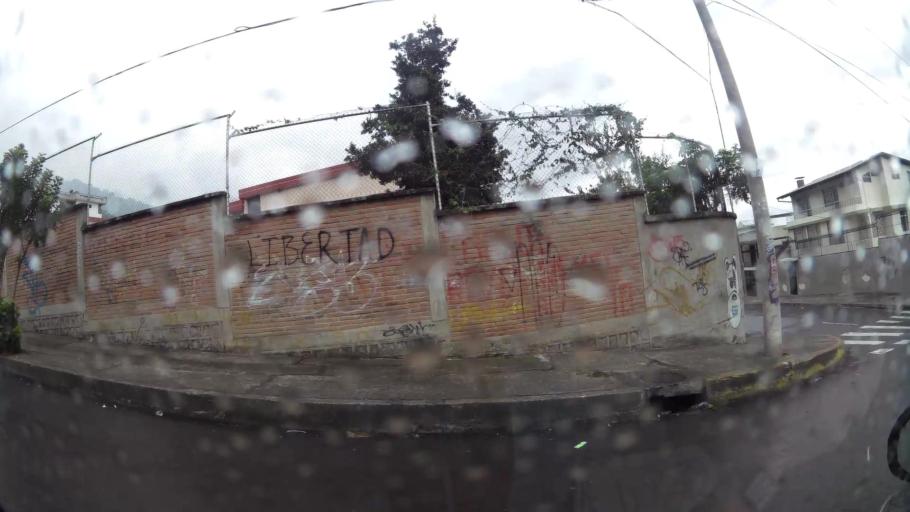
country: EC
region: Pichincha
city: Quito
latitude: -0.1982
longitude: -78.5095
